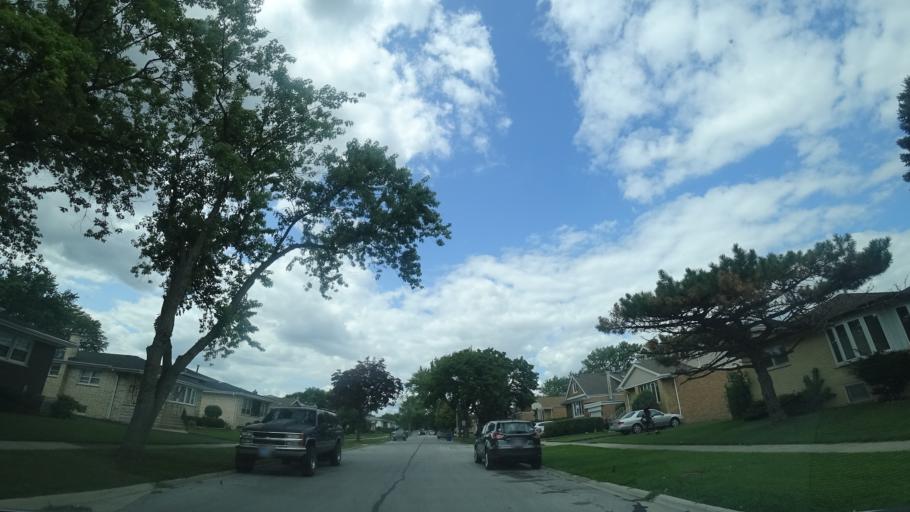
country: US
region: Illinois
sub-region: Cook County
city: Alsip
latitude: 41.6952
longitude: -87.7326
